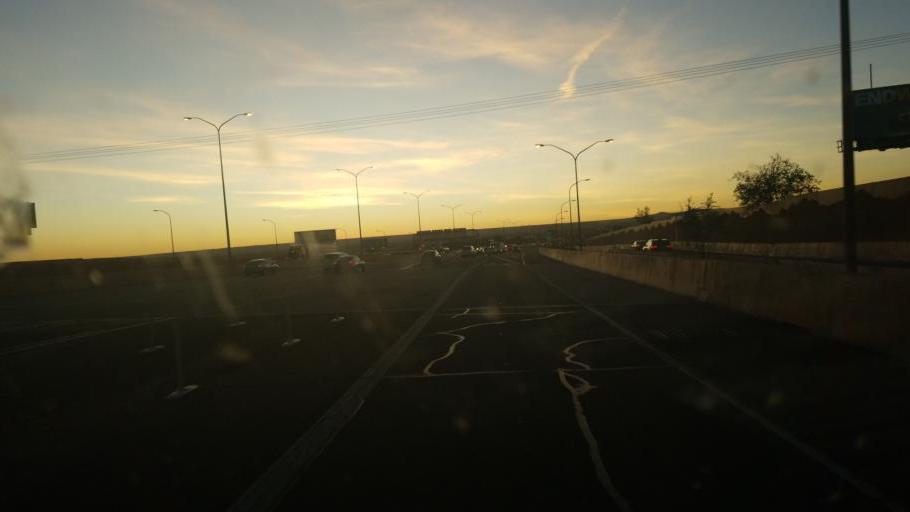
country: US
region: New Mexico
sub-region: Bernalillo County
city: Albuquerque
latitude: 35.1054
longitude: -106.6366
